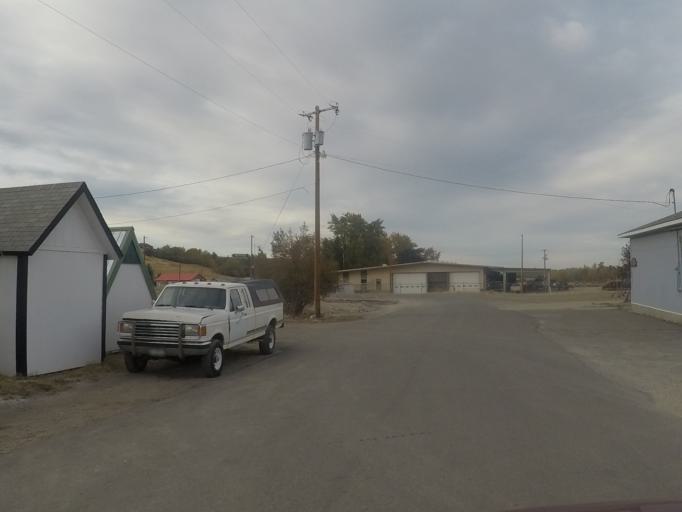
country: US
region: Montana
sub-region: Carbon County
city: Red Lodge
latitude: 45.1988
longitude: -109.2447
